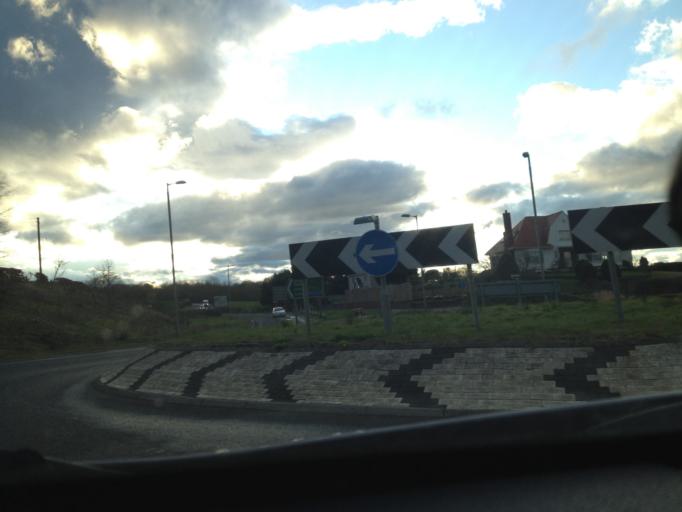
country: GB
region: Scotland
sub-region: South Lanarkshire
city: Dalserf
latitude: 55.7400
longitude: -3.9288
